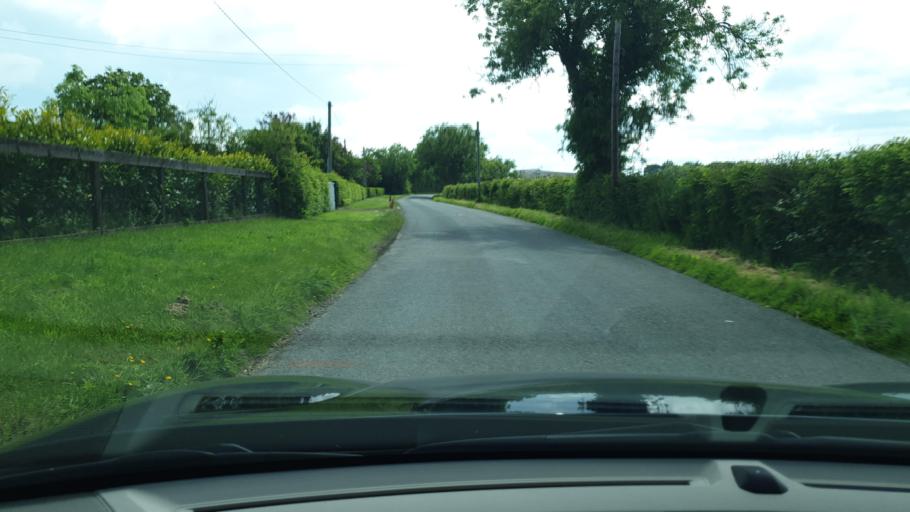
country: IE
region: Leinster
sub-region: An Mhi
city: Ratoath
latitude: 53.5706
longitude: -6.4499
